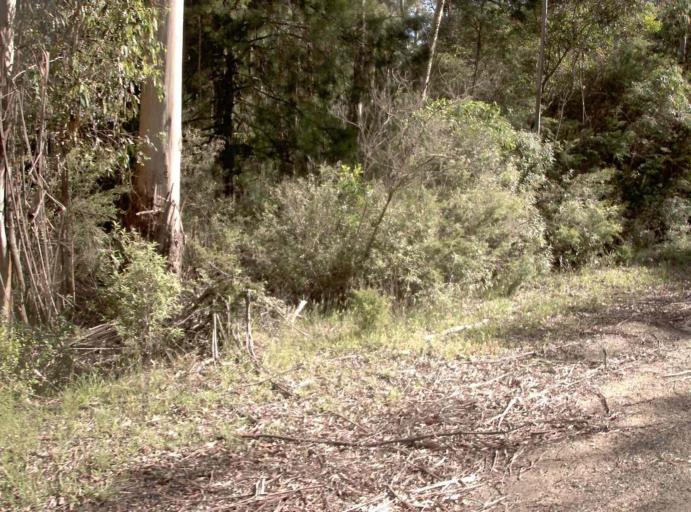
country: AU
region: Victoria
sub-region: East Gippsland
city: Lakes Entrance
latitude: -37.6671
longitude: 148.0675
